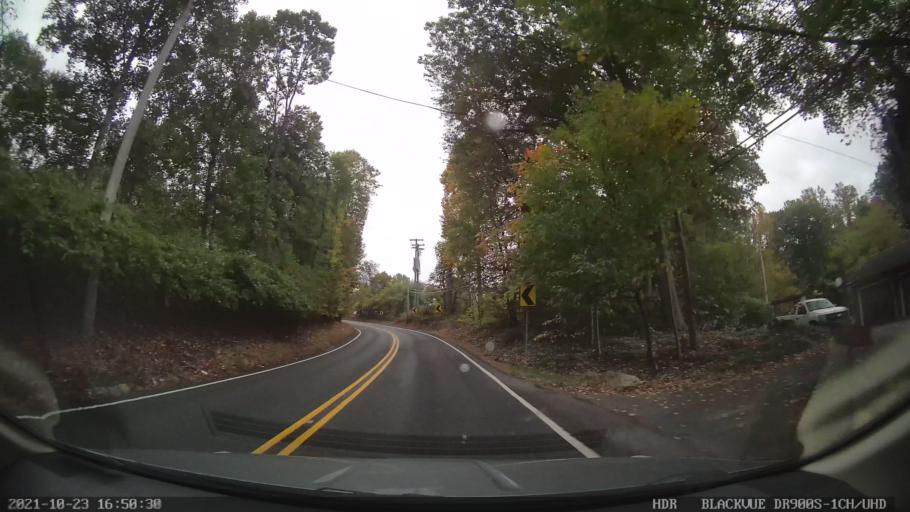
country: US
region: Pennsylvania
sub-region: Berks County
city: Red Lion
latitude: 40.4776
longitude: -75.6145
